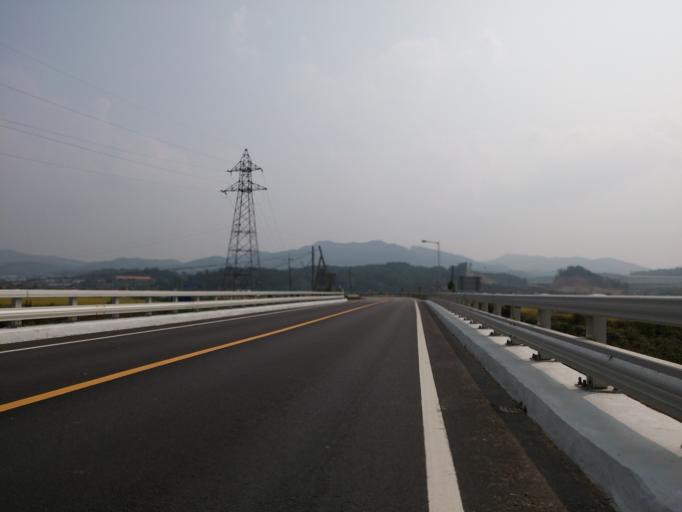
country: KR
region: Chungcheongbuk-do
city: Yong-dong
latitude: 36.3407
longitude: 127.7981
